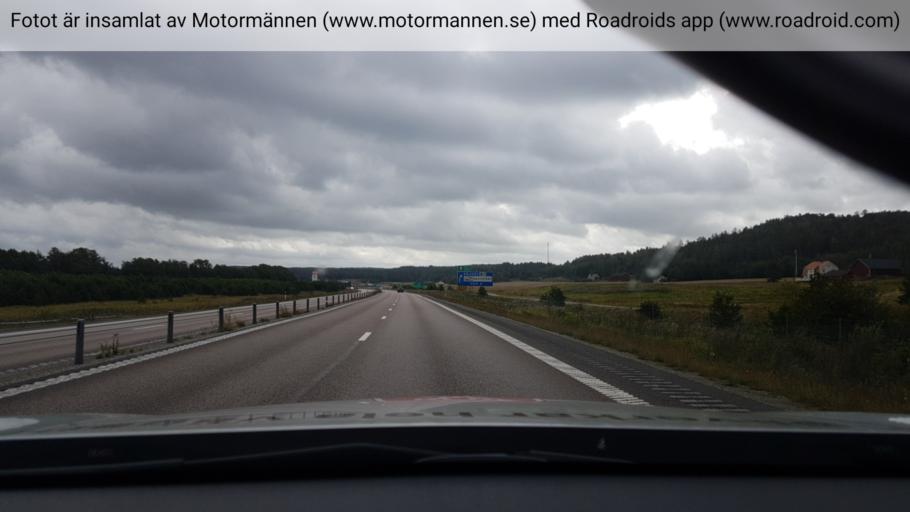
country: SE
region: Vaestra Goetaland
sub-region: Stromstads Kommun
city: Stroemstad
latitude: 58.9283
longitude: 11.2555
